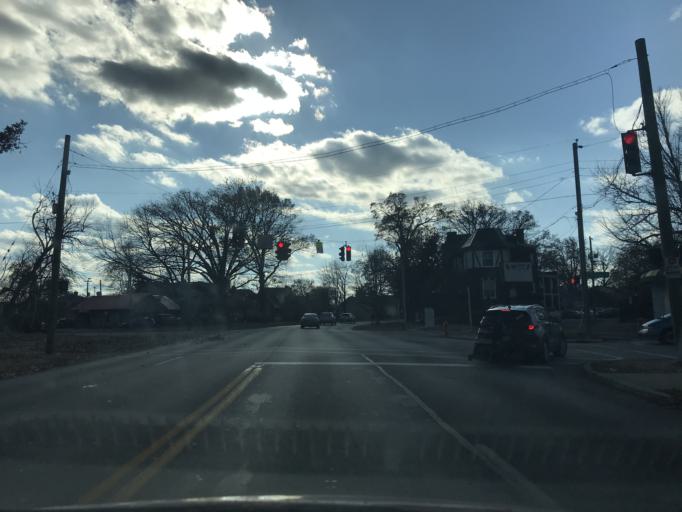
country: US
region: Kentucky
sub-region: Jefferson County
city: Audubon Park
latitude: 38.2127
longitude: -85.7470
